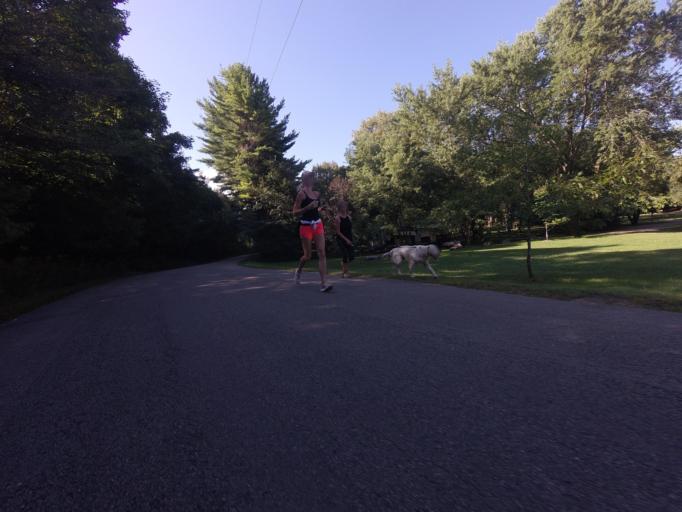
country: CA
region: Ontario
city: Waterloo
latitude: 43.6685
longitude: -80.4499
